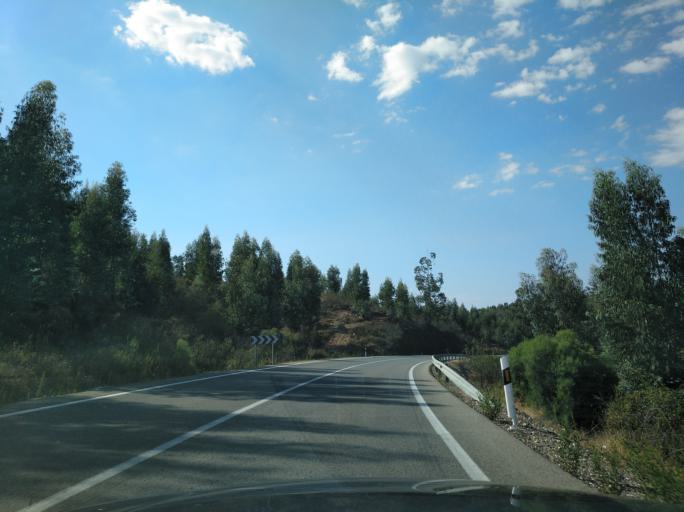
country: ES
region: Andalusia
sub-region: Provincia de Huelva
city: Santa Barbara de Casa
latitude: 37.8142
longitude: -7.2105
